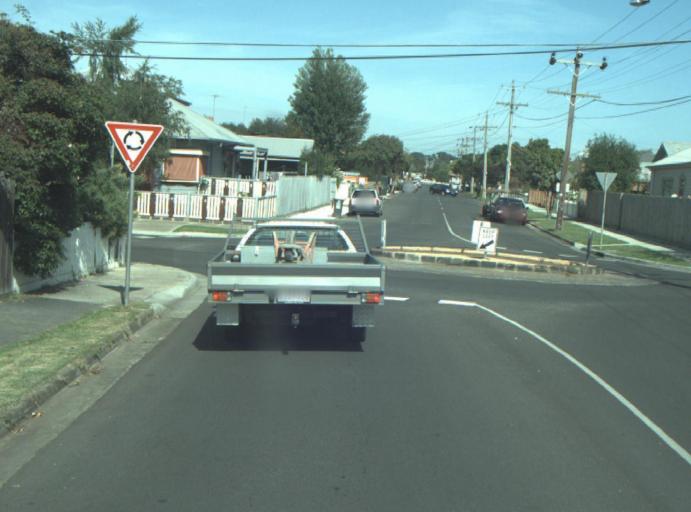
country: AU
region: Victoria
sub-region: Greater Geelong
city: Geelong West
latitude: -38.1438
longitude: 144.3391
